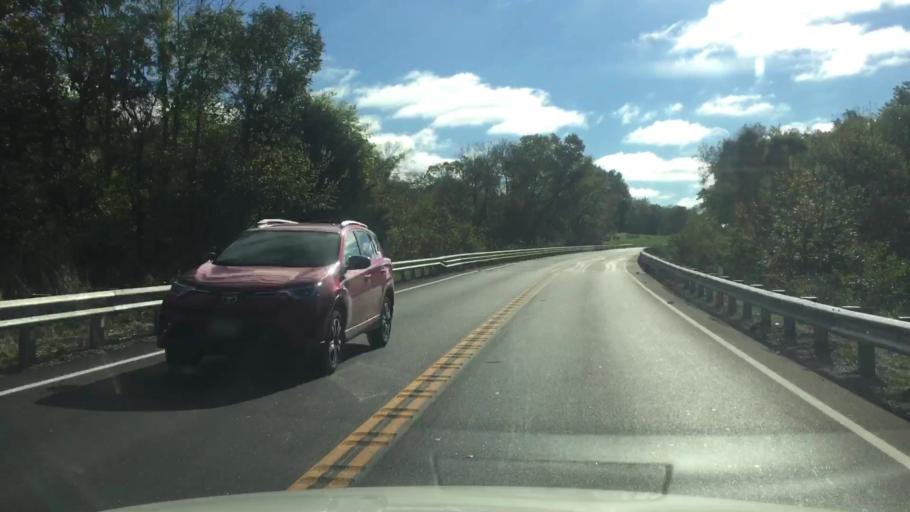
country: US
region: Missouri
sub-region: Howard County
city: New Franklin
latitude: 38.9934
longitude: -92.5657
